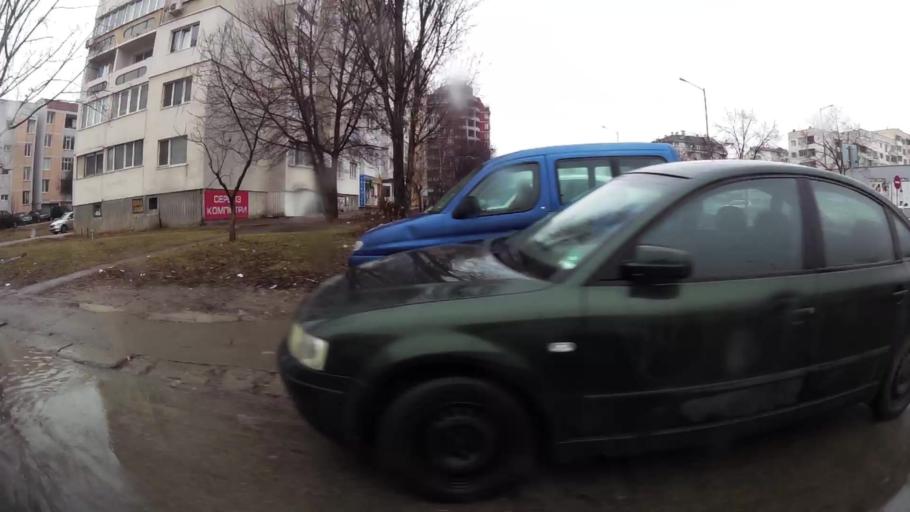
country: BG
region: Sofia-Capital
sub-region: Stolichna Obshtina
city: Sofia
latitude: 42.6351
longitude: 23.3776
